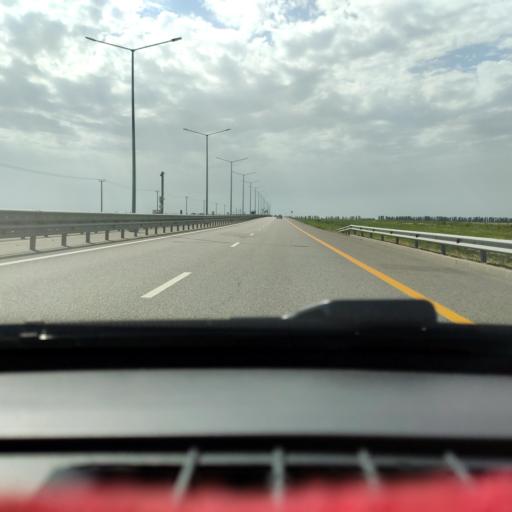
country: RU
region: Voronezj
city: Kashirskoye
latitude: 51.4918
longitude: 39.5297
